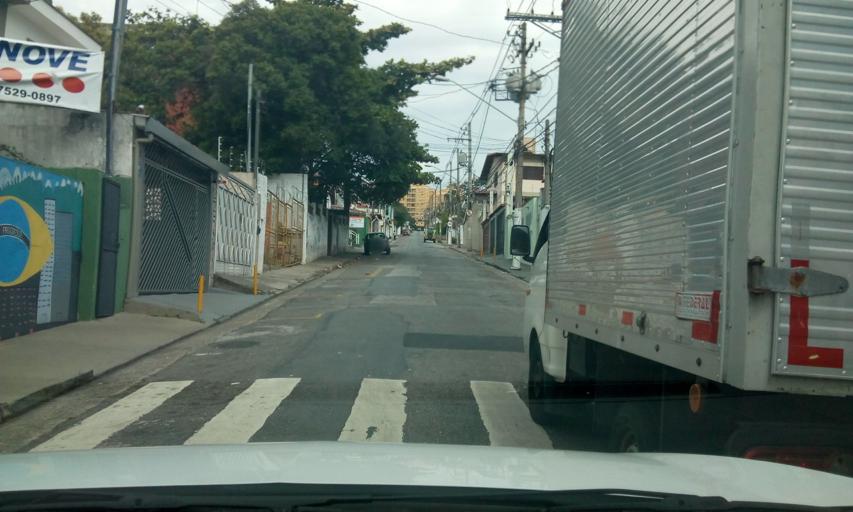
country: BR
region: Sao Paulo
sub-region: Taboao Da Serra
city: Taboao da Serra
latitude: -23.5905
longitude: -46.7282
